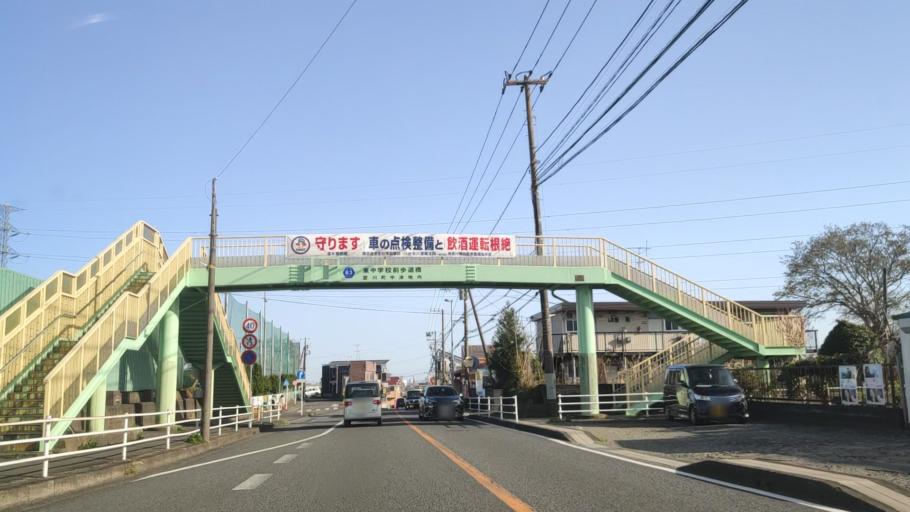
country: JP
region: Kanagawa
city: Zama
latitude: 35.5230
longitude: 139.3277
